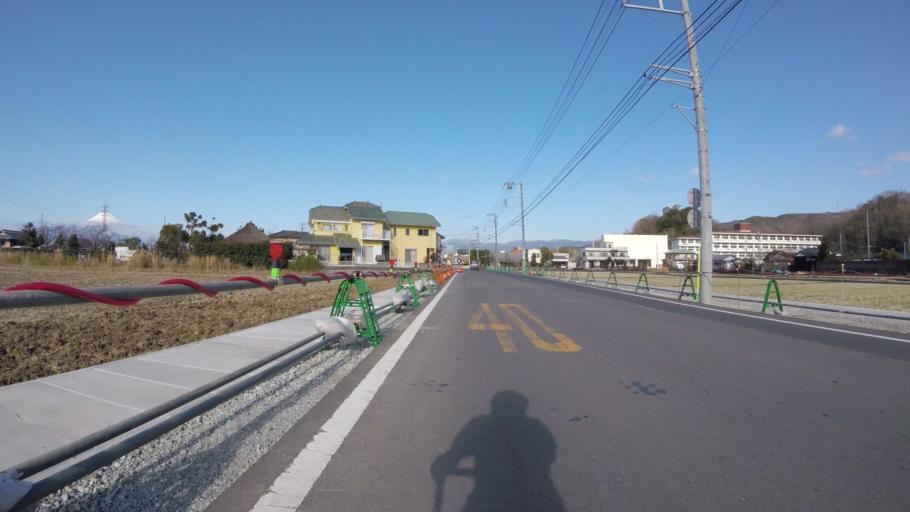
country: JP
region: Shizuoka
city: Mishima
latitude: 35.0511
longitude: 138.9524
